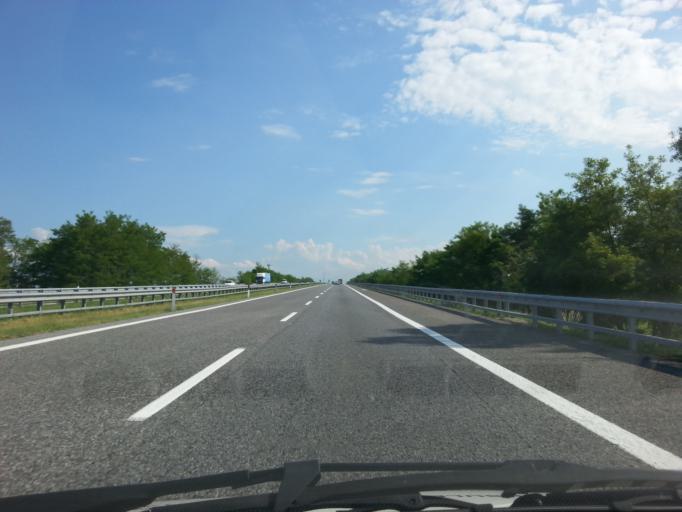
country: IT
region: Piedmont
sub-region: Provincia di Cuneo
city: Caramagna Piemonte
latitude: 44.8128
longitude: 7.7513
